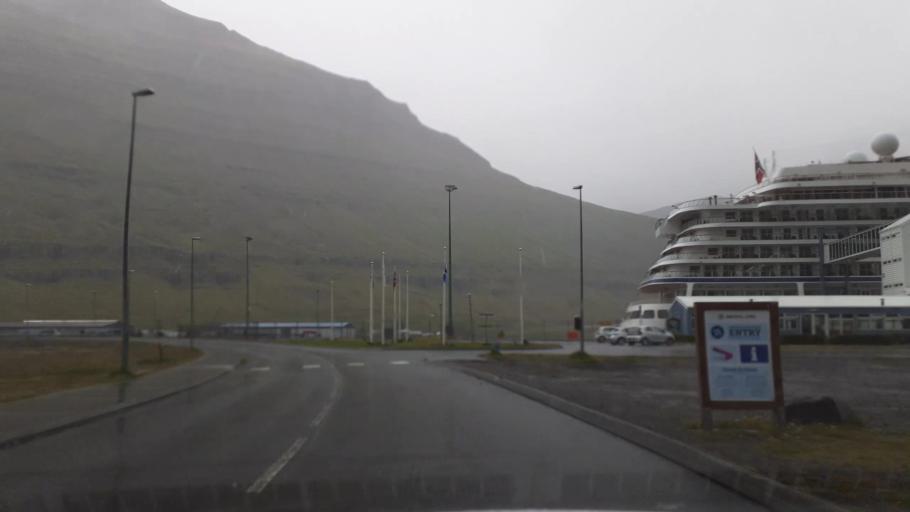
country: IS
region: East
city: Eskifjoerdur
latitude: 65.2625
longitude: -14.0019
